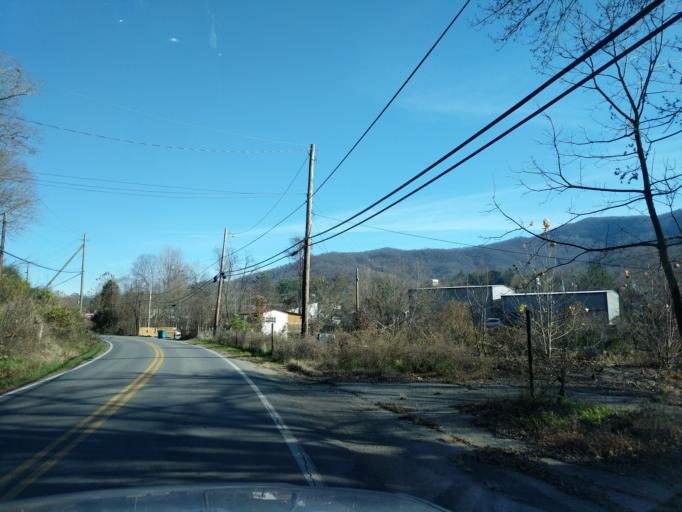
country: US
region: North Carolina
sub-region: Buncombe County
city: Swannanoa
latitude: 35.6021
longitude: -82.4010
